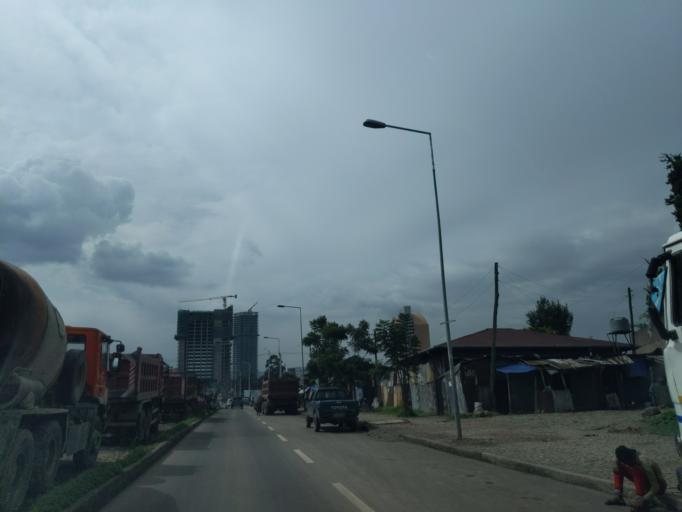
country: ET
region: Adis Abeba
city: Addis Ababa
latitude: 9.0063
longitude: 38.7546
